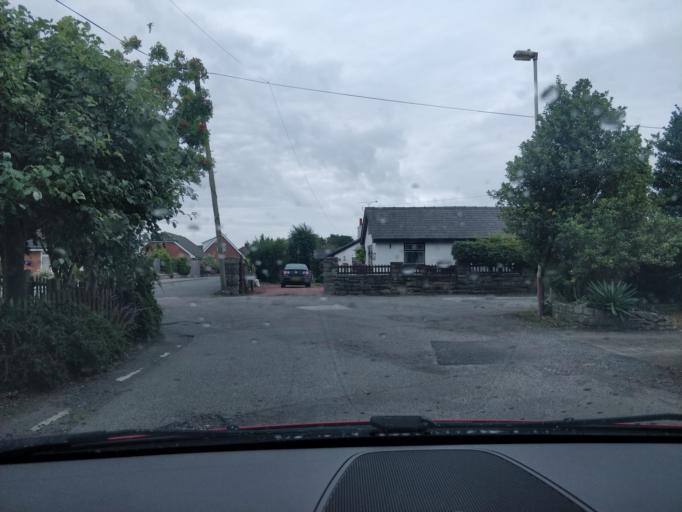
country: GB
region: England
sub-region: Sefton
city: Southport
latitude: 53.6669
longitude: -2.9714
